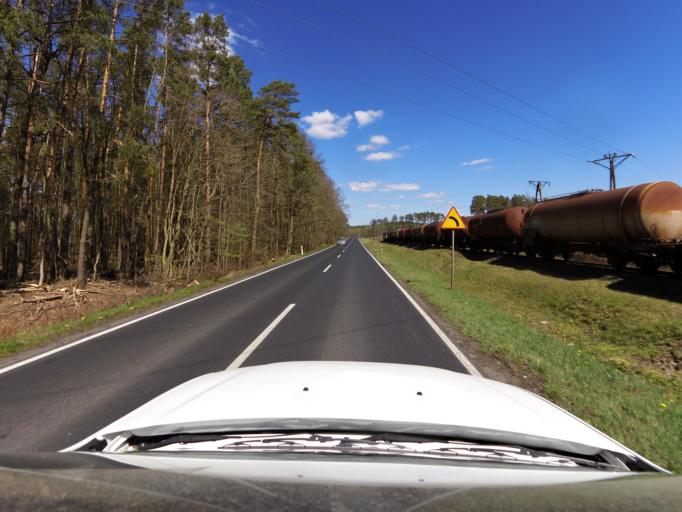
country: PL
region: West Pomeranian Voivodeship
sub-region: Powiat mysliborski
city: Debno
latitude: 52.7571
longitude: 14.7339
